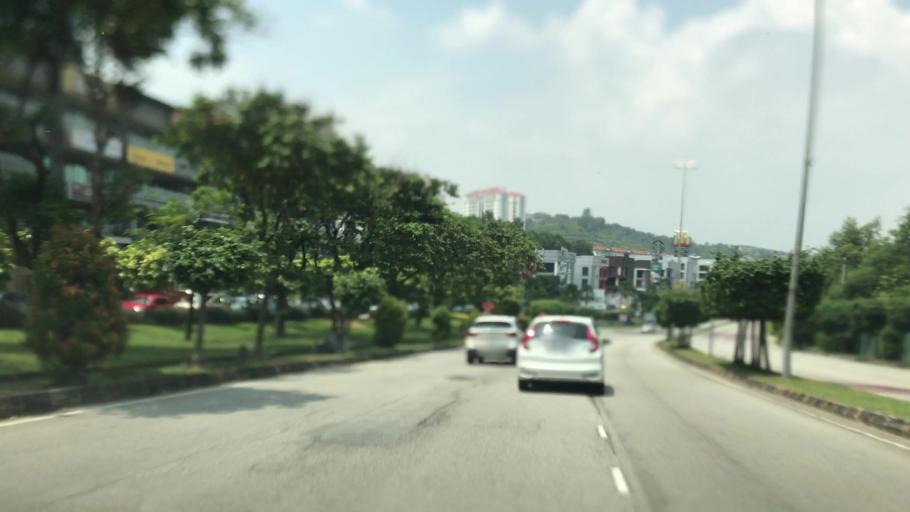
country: MY
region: Selangor
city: Subang Jaya
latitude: 3.0224
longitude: 101.6234
